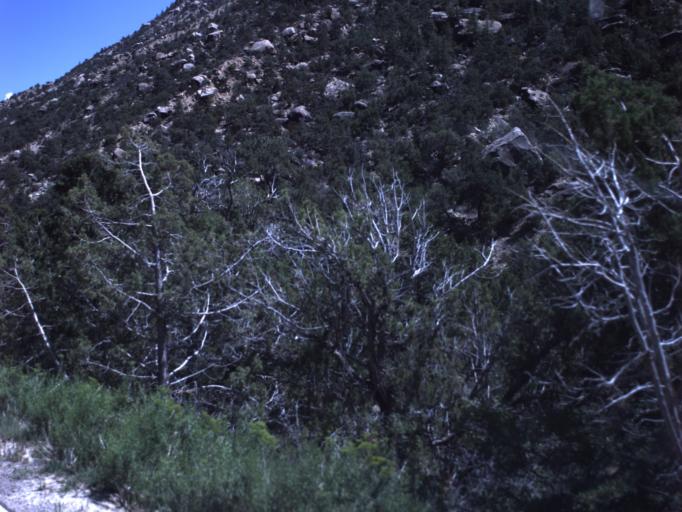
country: US
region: Utah
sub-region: Emery County
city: Orangeville
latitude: 39.2739
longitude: -111.1917
